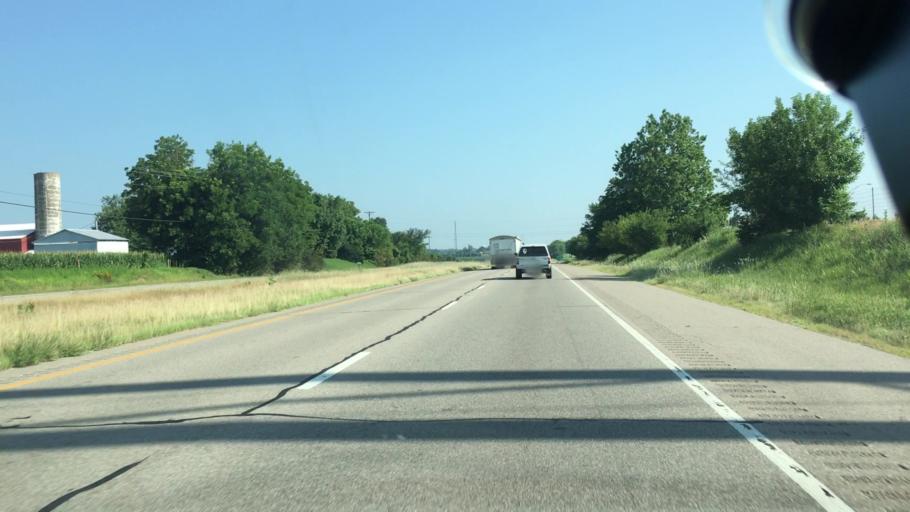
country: US
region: Indiana
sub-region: Gibson County
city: Fort Branch
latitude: 38.2905
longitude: -87.5674
